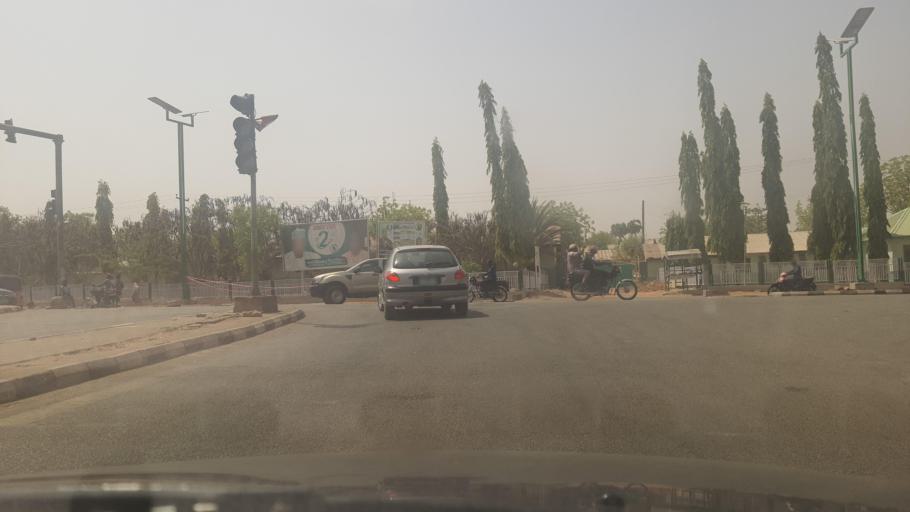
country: NG
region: Gombe
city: Gombe
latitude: 10.2834
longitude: 11.1534
